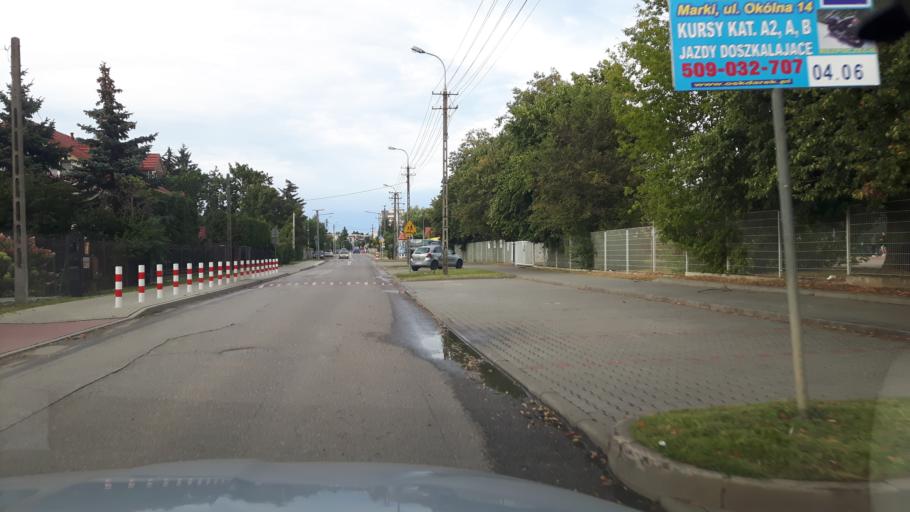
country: PL
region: Masovian Voivodeship
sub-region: Powiat wolominski
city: Marki
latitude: 52.3240
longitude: 21.0980
